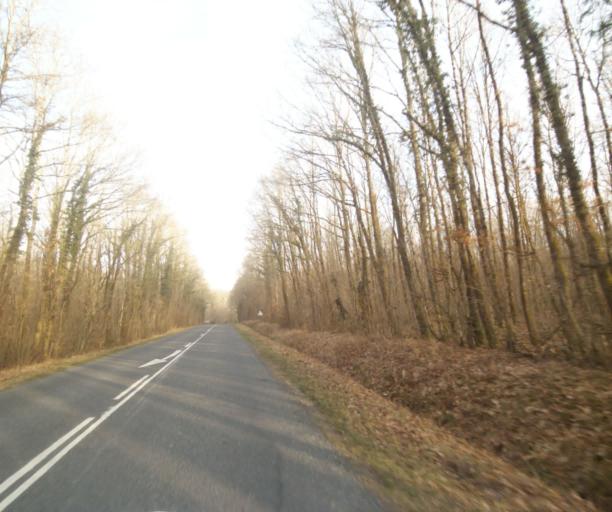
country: FR
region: Champagne-Ardenne
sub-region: Departement de la Haute-Marne
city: Bettancourt-la-Ferree
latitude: 48.6772
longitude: 4.9416
